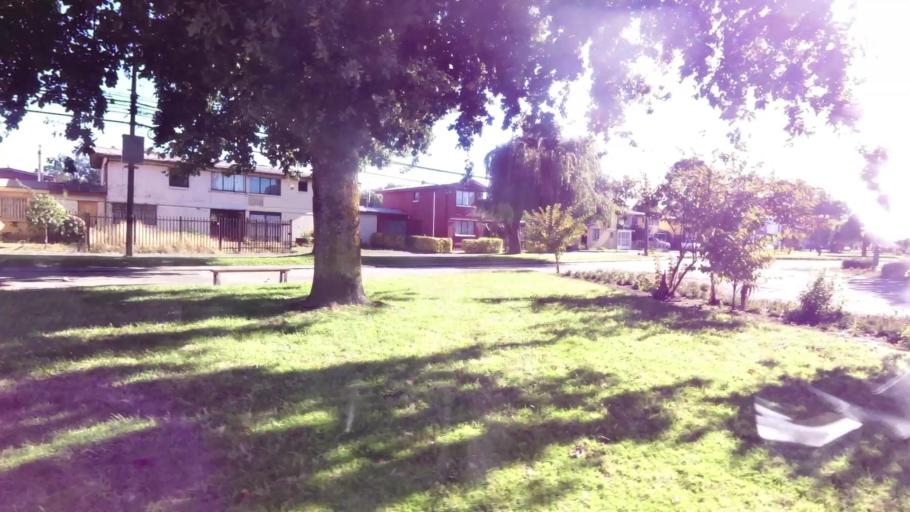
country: CL
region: Biobio
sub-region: Provincia de Concepcion
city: Concepcion
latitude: -36.8403
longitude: -73.1051
